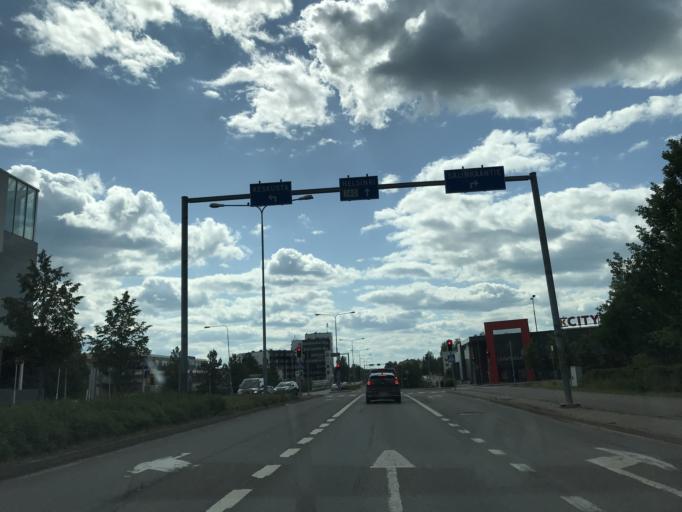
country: FI
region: Uusimaa
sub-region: Helsinki
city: Maentsaelae
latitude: 60.6379
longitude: 25.3194
